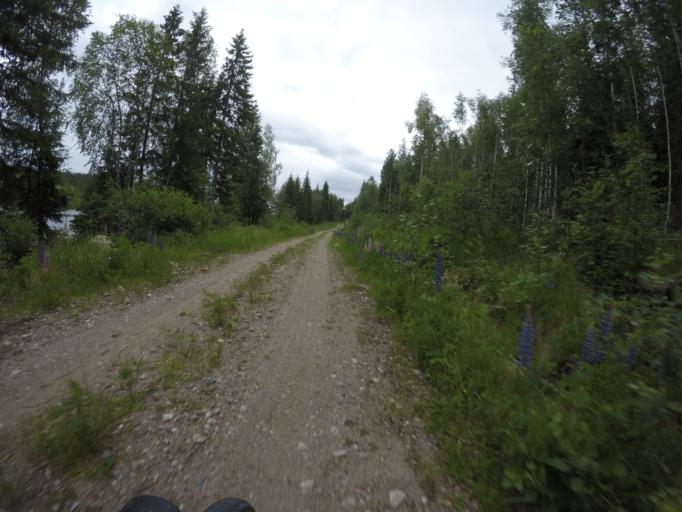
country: SE
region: Dalarna
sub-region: Ludvika Kommun
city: Abborrberget
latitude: 60.0454
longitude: 14.5916
